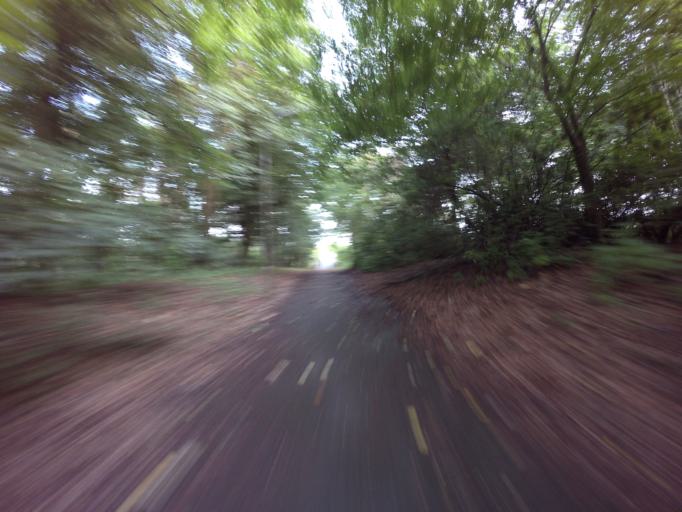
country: GB
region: Scotland
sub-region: West Lothian
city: Livingston
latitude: 55.9126
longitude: -3.5619
